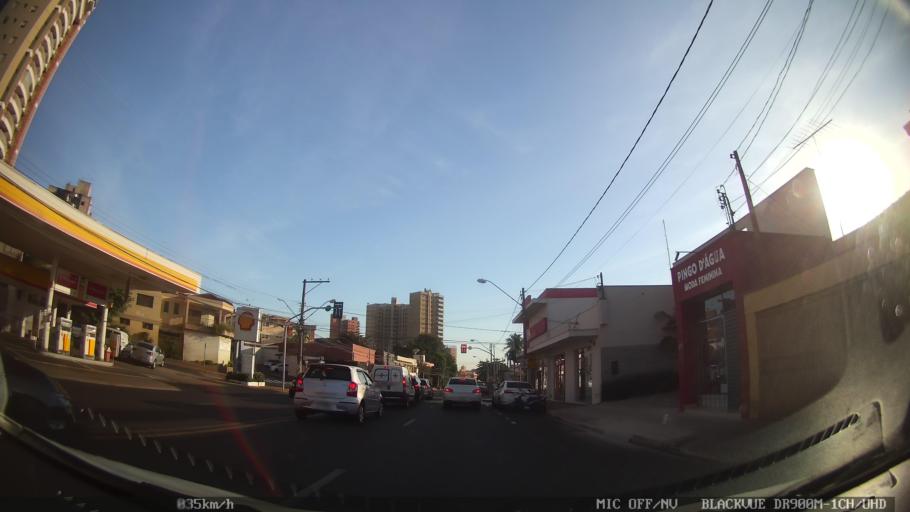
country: BR
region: Sao Paulo
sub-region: Ribeirao Preto
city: Ribeirao Preto
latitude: -21.1908
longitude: -47.8012
